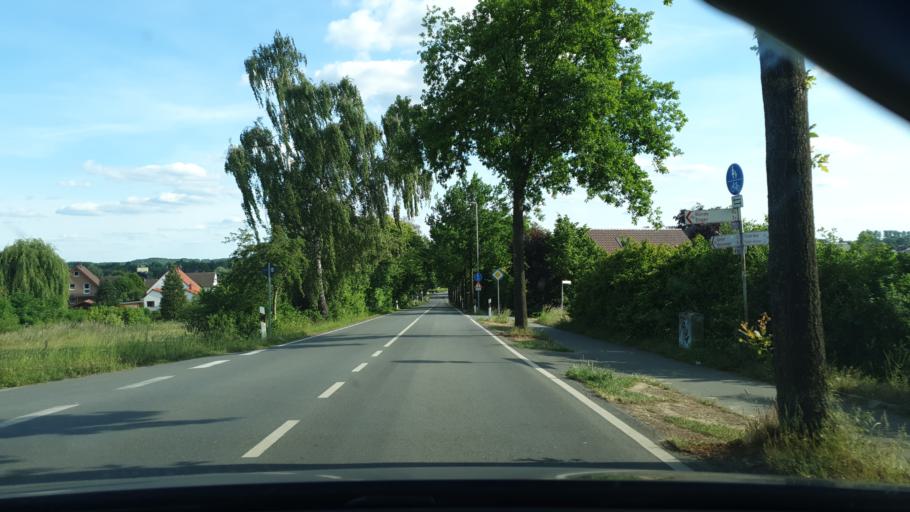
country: DE
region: North Rhine-Westphalia
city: Spenge
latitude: 52.1473
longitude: 8.5149
